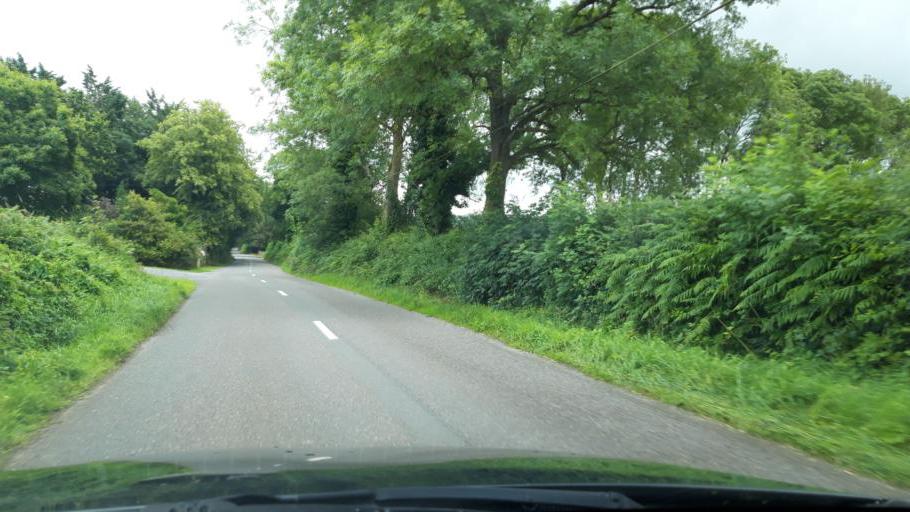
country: IE
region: Munster
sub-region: County Cork
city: Youghal
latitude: 52.1304
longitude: -7.9875
